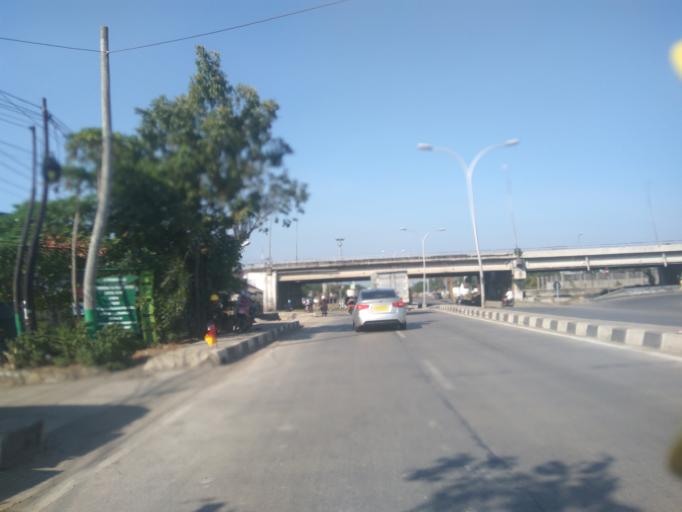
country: ID
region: Central Java
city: Semarang
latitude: -6.9571
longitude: 110.4508
